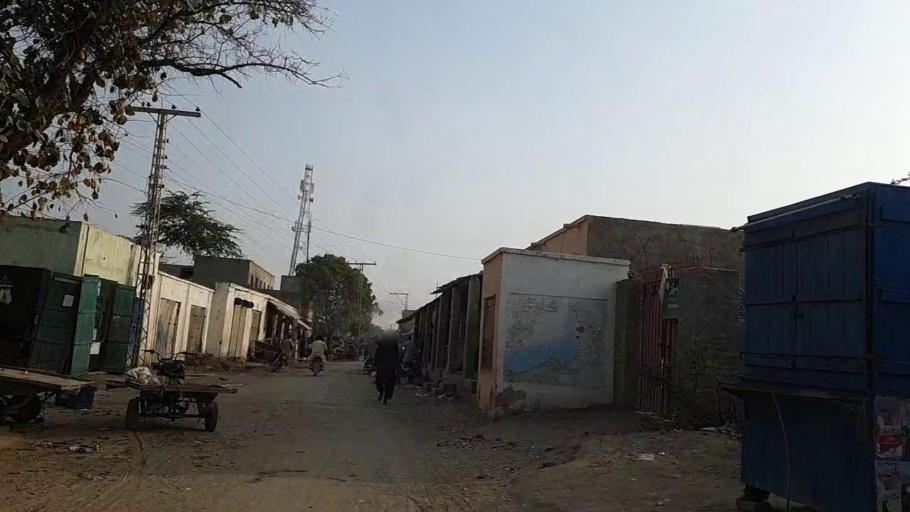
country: PK
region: Sindh
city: Naukot
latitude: 24.6596
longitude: 69.2895
